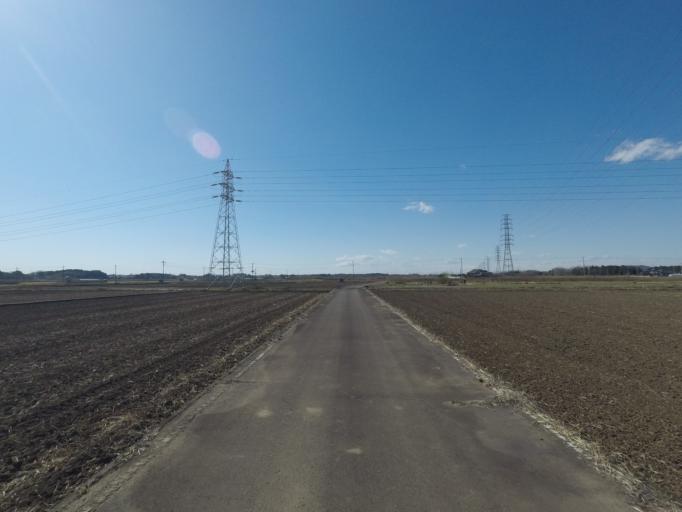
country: JP
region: Ibaraki
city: Tsukuba
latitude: 36.1371
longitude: 140.1173
